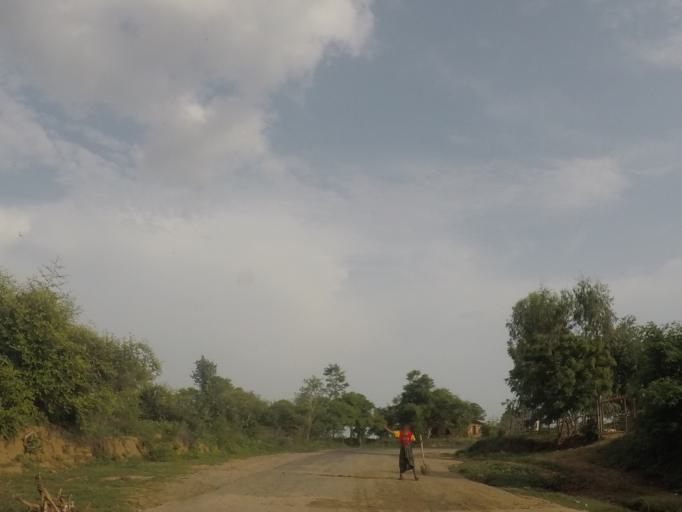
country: MM
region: Mandalay
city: Meiktila
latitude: 20.5074
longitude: 95.6112
